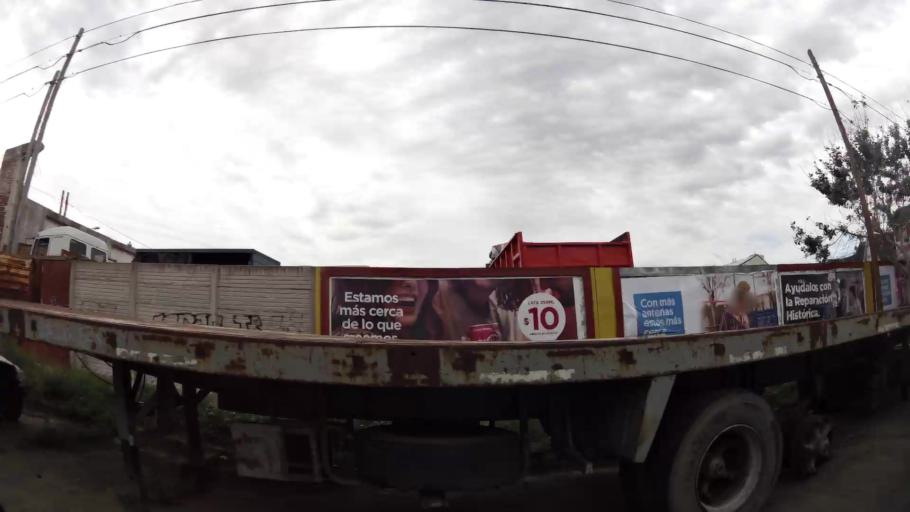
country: AR
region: Buenos Aires
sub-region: Partido de Lanus
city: Lanus
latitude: -34.6778
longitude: -58.3924
